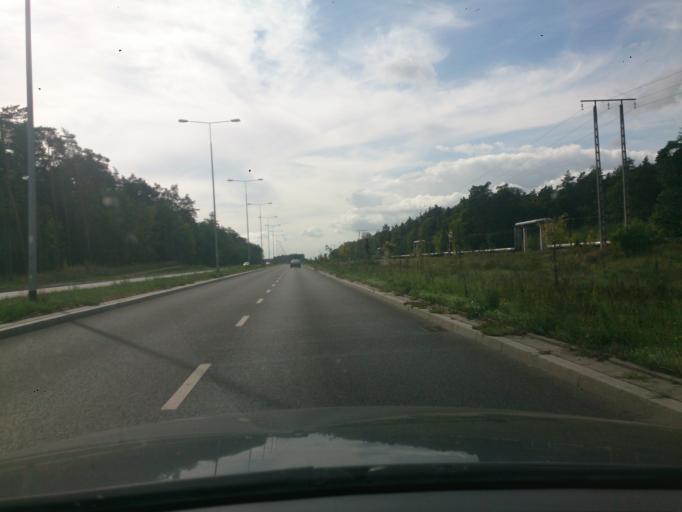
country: PL
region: Kujawsko-Pomorskie
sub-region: Grudziadz
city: Grudziadz
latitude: 53.4591
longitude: 18.7422
